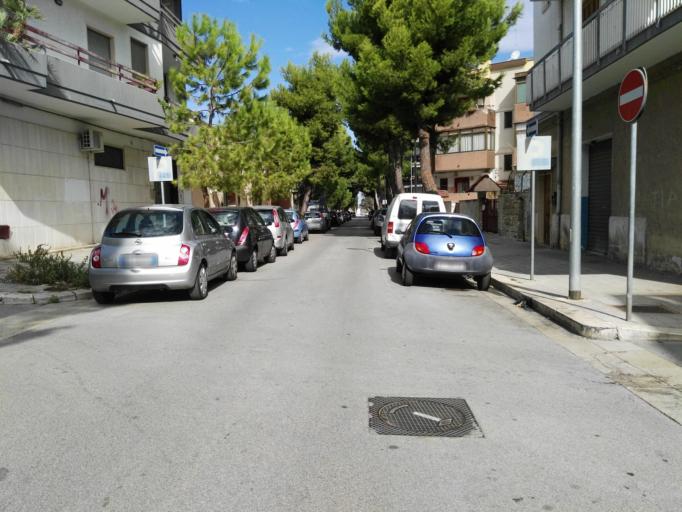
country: IT
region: Apulia
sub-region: Provincia di Bari
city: Triggiano
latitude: 41.0643
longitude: 16.9170
